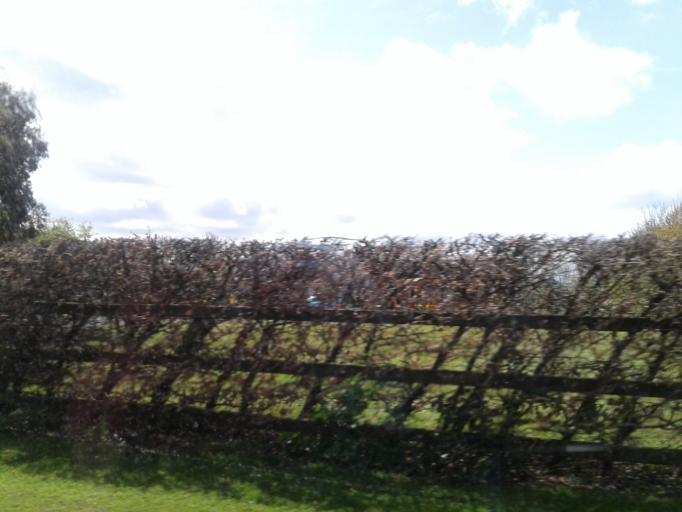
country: IE
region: Leinster
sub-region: Fingal County
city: Swords
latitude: 53.4706
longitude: -6.2463
